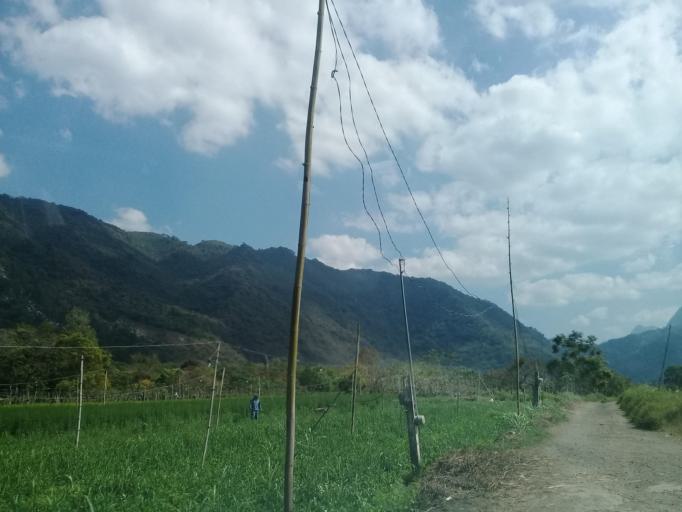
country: MX
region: Veracruz
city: Jalapilla
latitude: 18.8285
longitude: -97.0691
